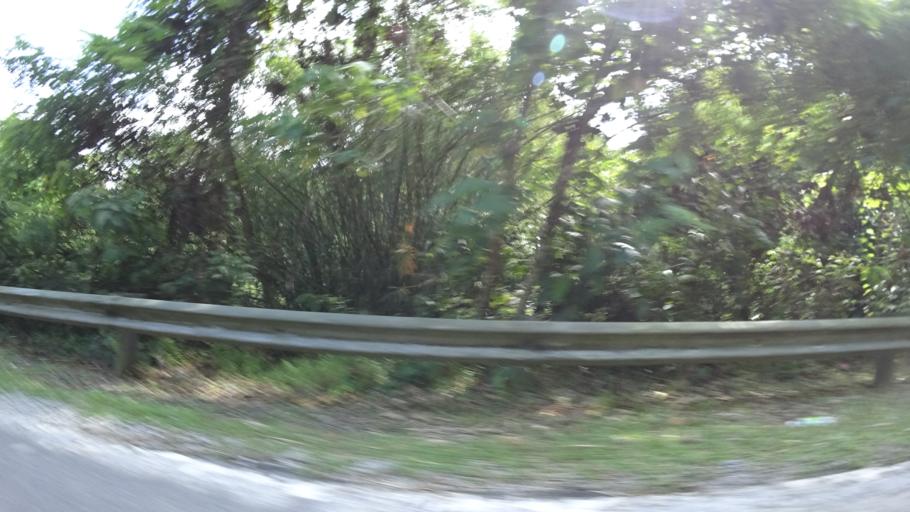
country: BN
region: Brunei and Muara
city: Bandar Seri Begawan
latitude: 4.8810
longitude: 114.9633
